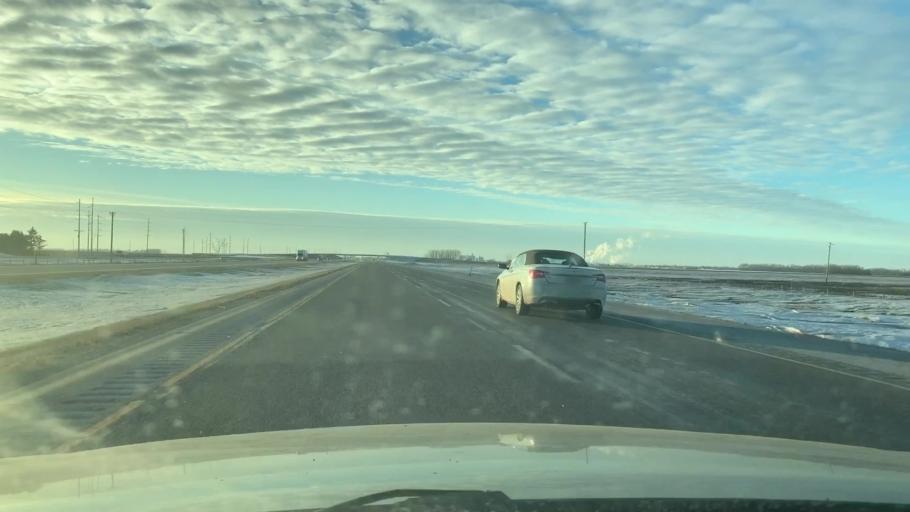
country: US
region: North Dakota
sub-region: Cass County
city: Casselton
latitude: 46.8768
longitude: -97.1459
